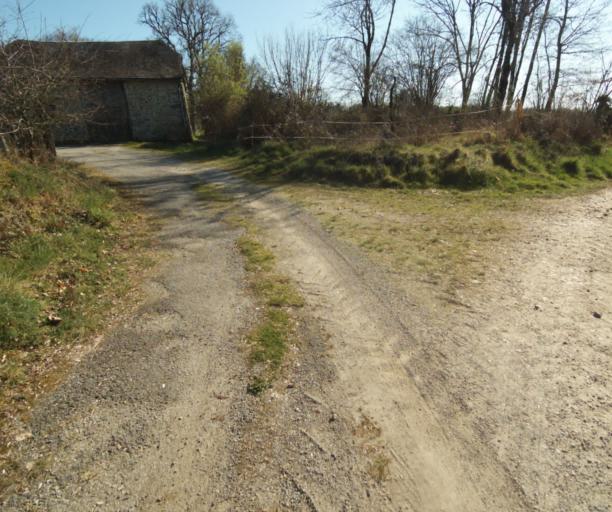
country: FR
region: Limousin
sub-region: Departement de la Correze
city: Chamboulive
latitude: 45.4860
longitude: 1.7097
